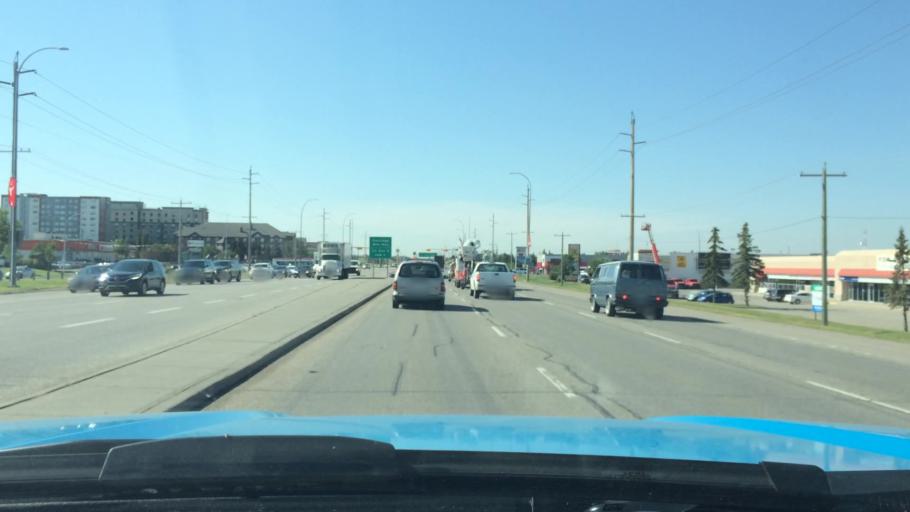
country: CA
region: Alberta
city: Calgary
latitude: 51.0756
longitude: -114.0017
